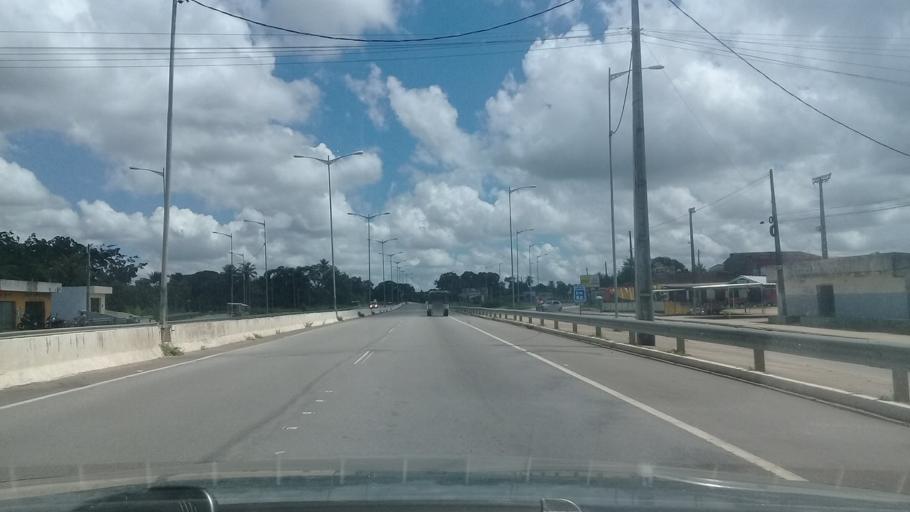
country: BR
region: Pernambuco
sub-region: Sao Lourenco Da Mata
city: Sao Lourenco da Mata
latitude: -7.9420
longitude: -35.1226
